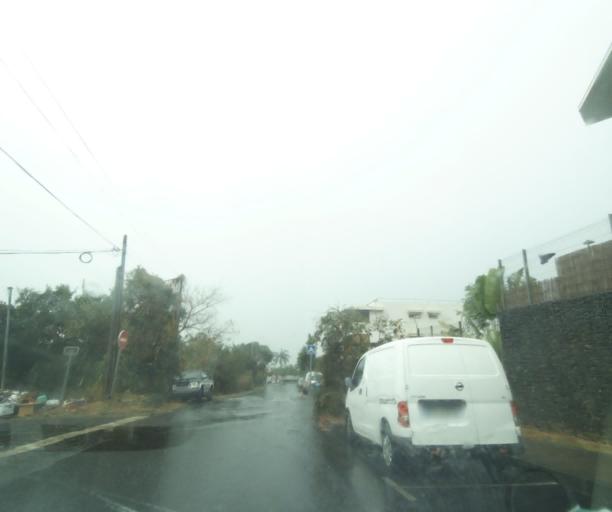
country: RE
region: Reunion
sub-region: Reunion
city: Saint-Paul
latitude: -20.9902
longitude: 55.3263
